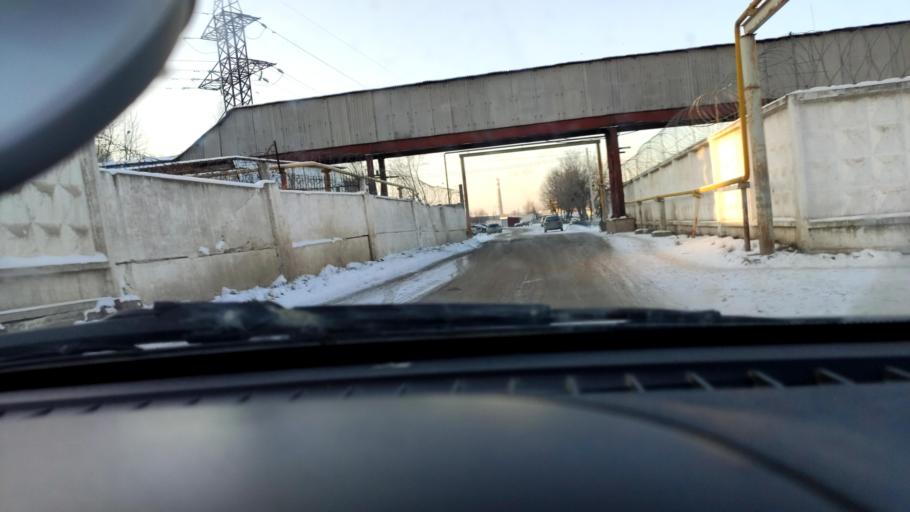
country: RU
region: Perm
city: Perm
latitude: 58.0717
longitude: 56.3531
